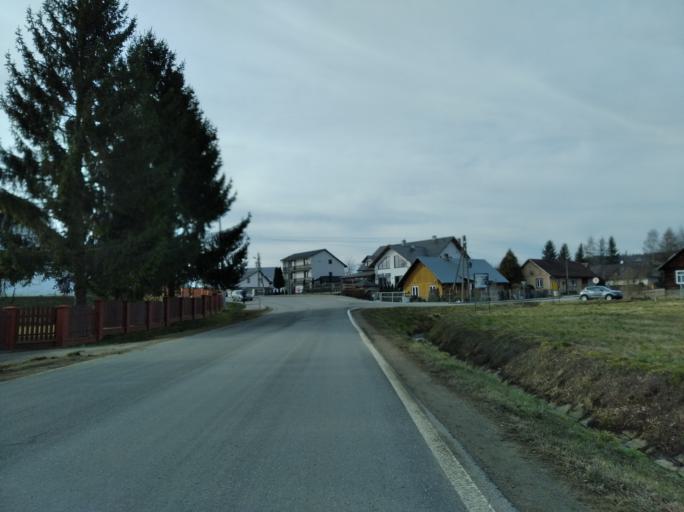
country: PL
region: Subcarpathian Voivodeship
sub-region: Powiat brzozowski
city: Turze Pole
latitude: 49.6621
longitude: 22.0041
